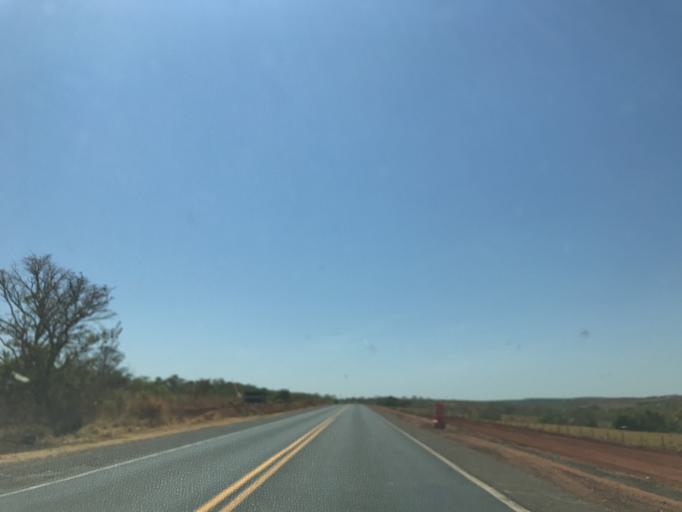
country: BR
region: Minas Gerais
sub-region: Prata
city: Prata
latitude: -19.4306
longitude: -48.8890
